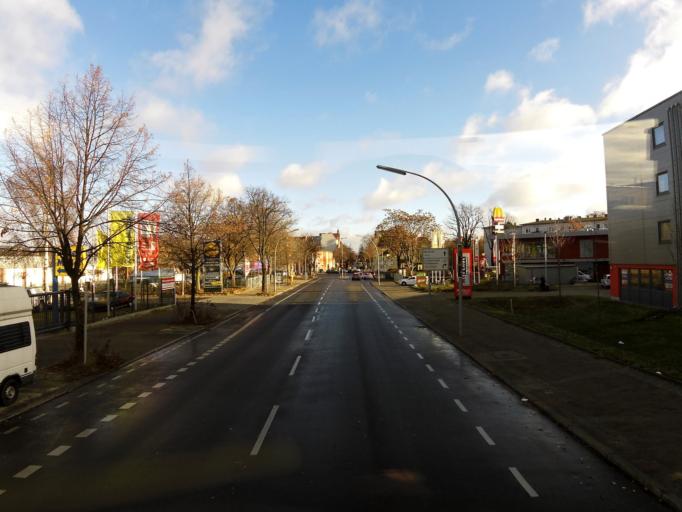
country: DE
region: Berlin
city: Mariendorf
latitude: 52.4375
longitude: 13.3783
